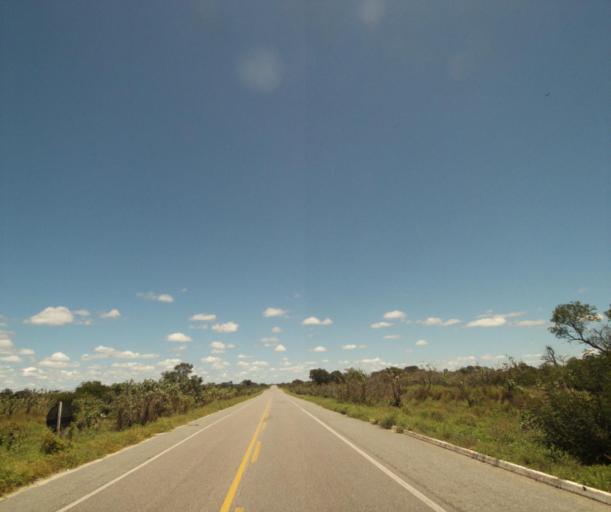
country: BR
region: Bahia
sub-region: Carinhanha
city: Carinhanha
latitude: -14.3123
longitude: -43.7851
